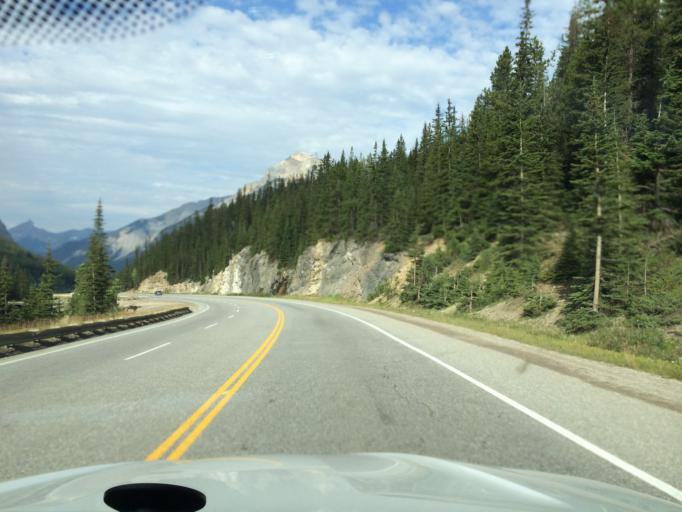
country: CA
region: Alberta
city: Lake Louise
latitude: 51.4366
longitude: -116.3834
